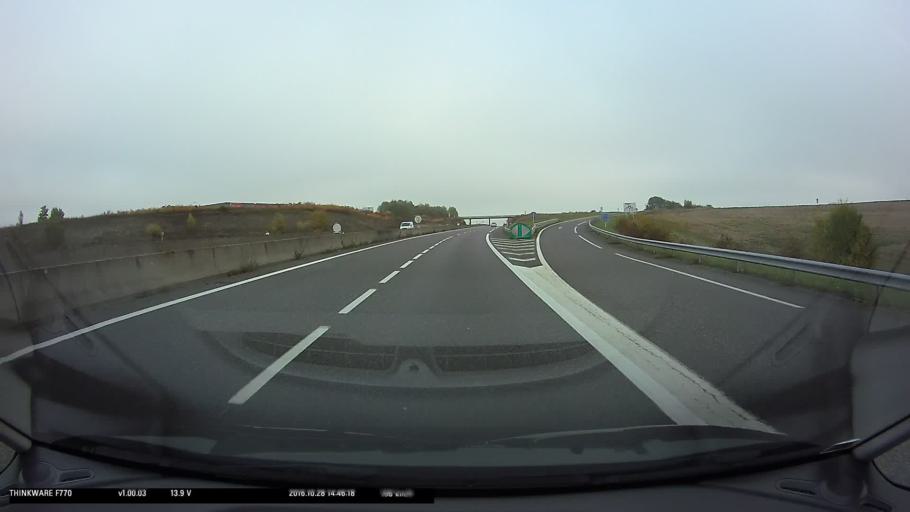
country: FR
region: Lorraine
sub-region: Departement de la Moselle
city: Sarrebourg
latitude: 48.7155
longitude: 7.0432
